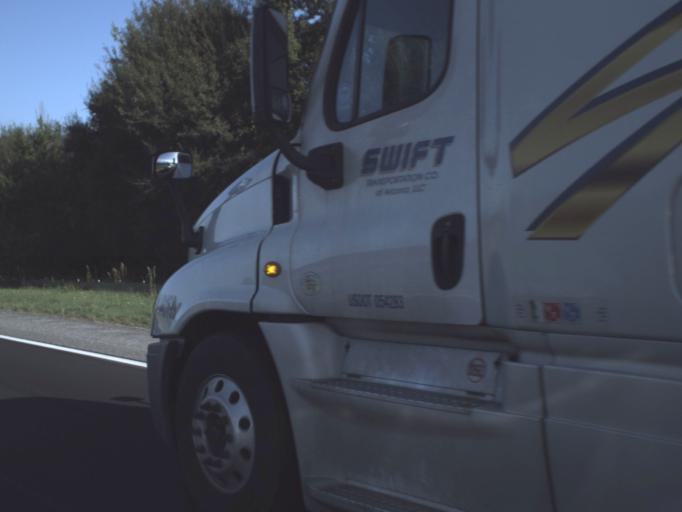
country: US
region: Florida
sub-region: Osceola County
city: Saint Cloud
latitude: 28.0449
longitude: -81.2117
